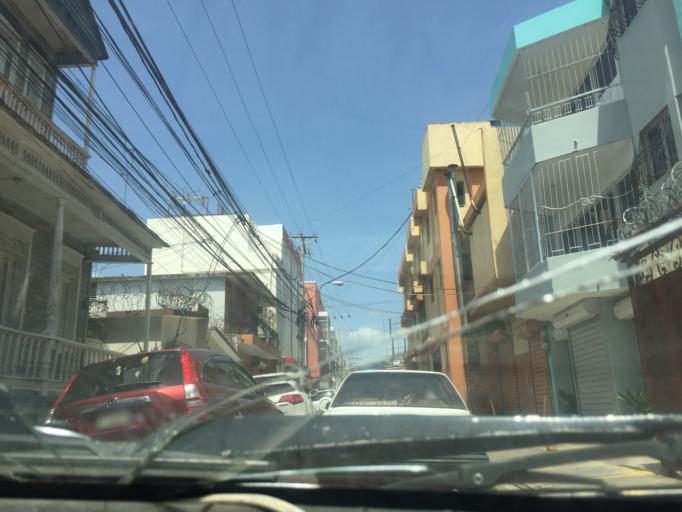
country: DO
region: Santiago
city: Santiago de los Caballeros
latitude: 19.4540
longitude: -70.7060
